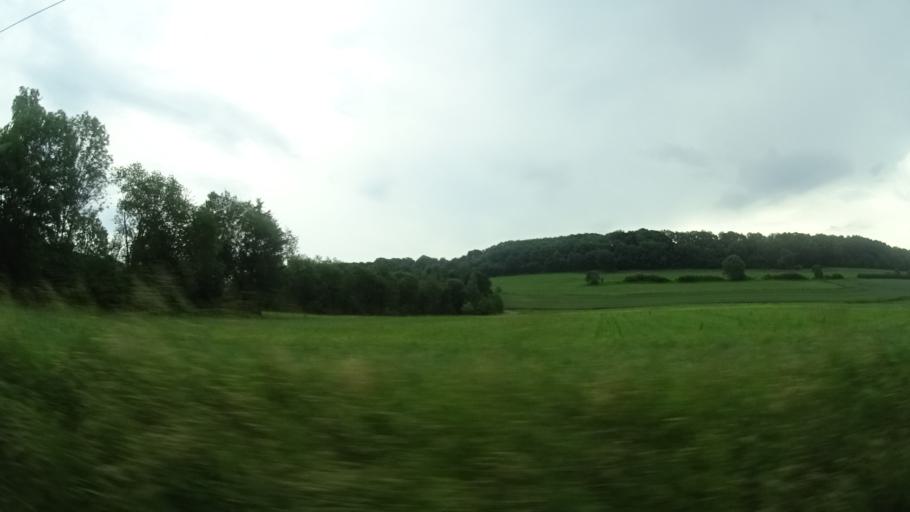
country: DE
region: Lower Saxony
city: Pegestorf
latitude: 51.9027
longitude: 9.4710
